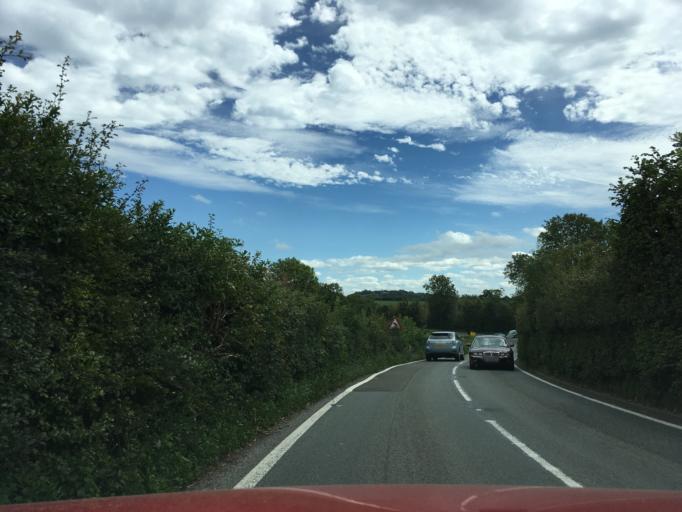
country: GB
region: England
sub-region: Somerset
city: Wells
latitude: 51.2171
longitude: -2.6895
